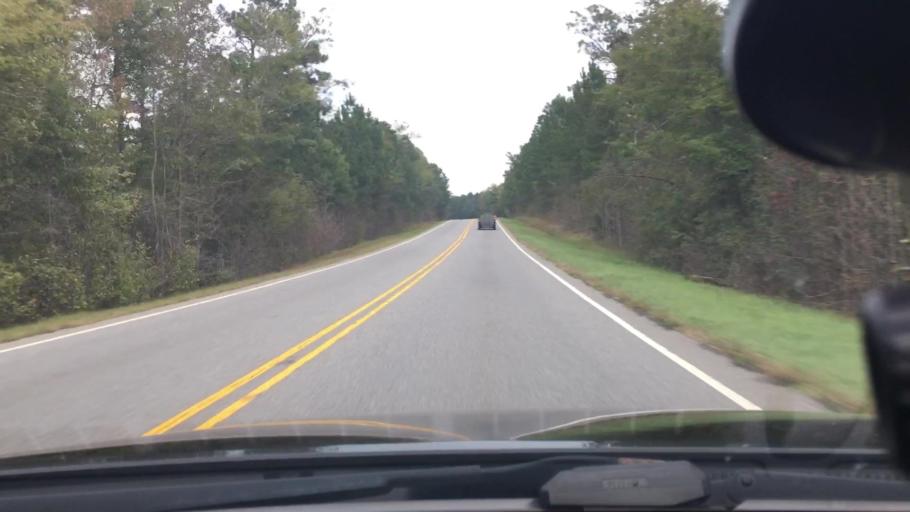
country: US
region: North Carolina
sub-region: Montgomery County
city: Biscoe
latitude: 35.3639
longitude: -79.6855
